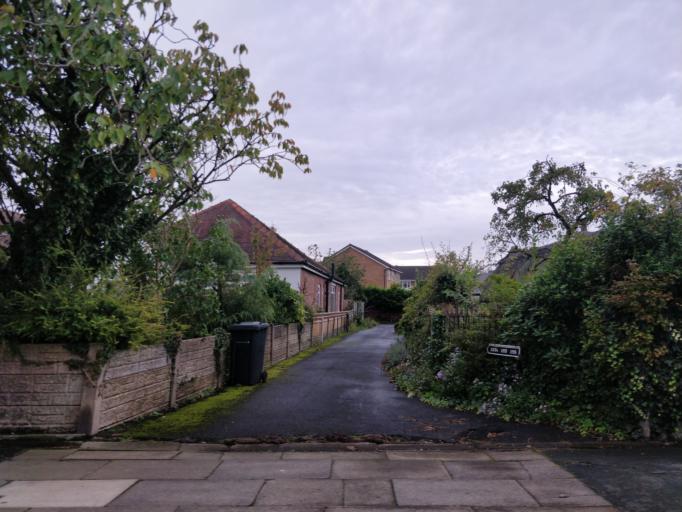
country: GB
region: England
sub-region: Sefton
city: Southport
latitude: 53.6680
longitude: -2.9713
